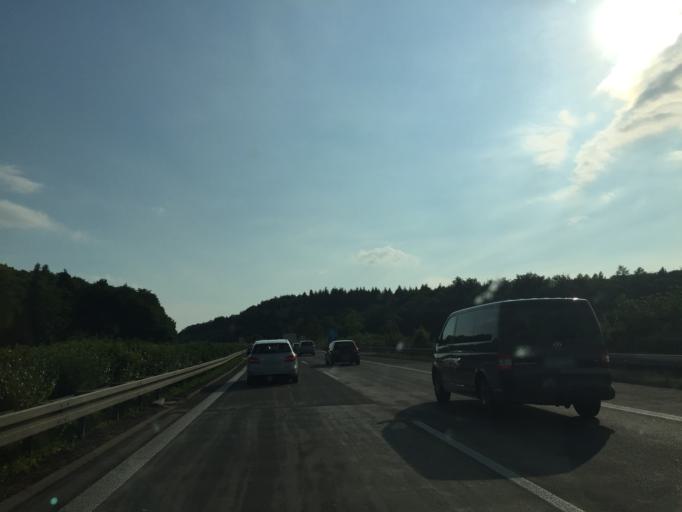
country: DE
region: Baden-Wuerttemberg
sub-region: Regierungsbezirk Stuttgart
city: Konigheim
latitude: 49.5605
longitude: 9.6190
